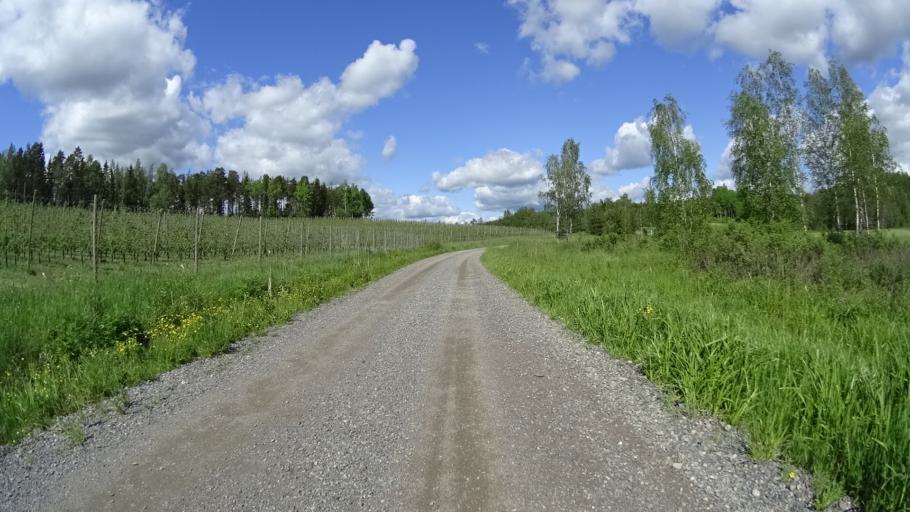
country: FI
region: Uusimaa
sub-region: Raaseporin
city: Karis
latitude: 60.1264
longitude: 23.6125
